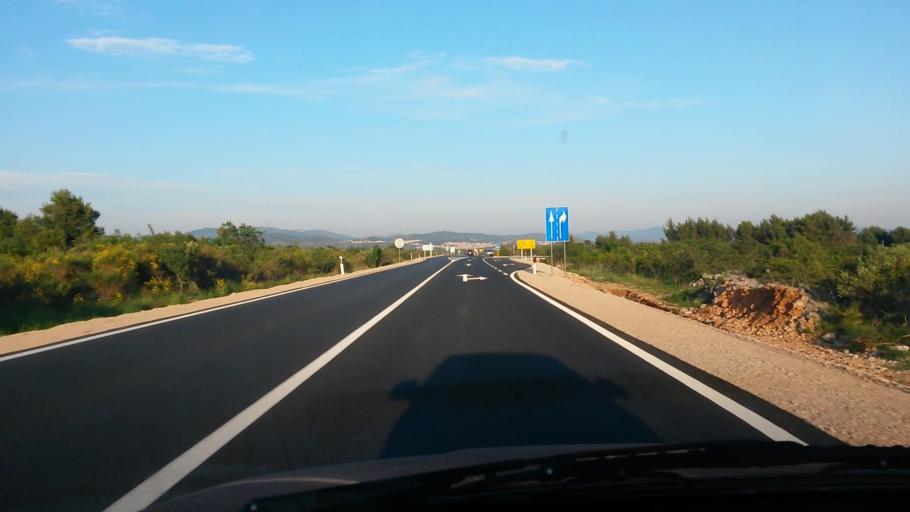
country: HR
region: Sibensko-Kniniska
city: Vodice
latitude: 43.7652
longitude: 15.8105
